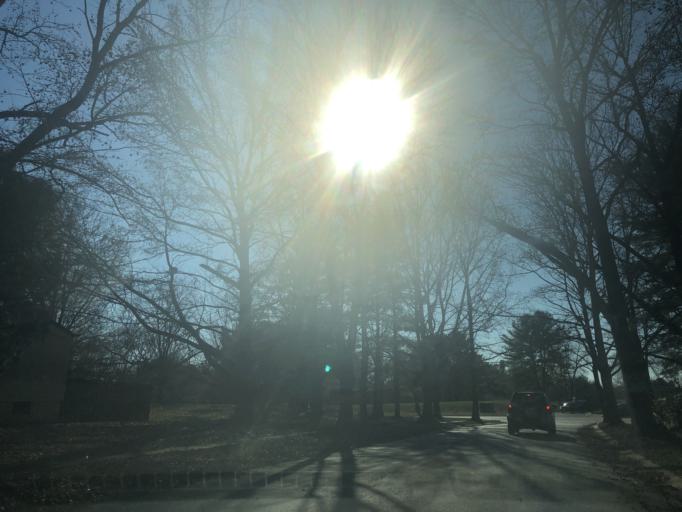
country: US
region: Maryland
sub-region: Howard County
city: Columbia
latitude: 39.1952
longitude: -76.8403
